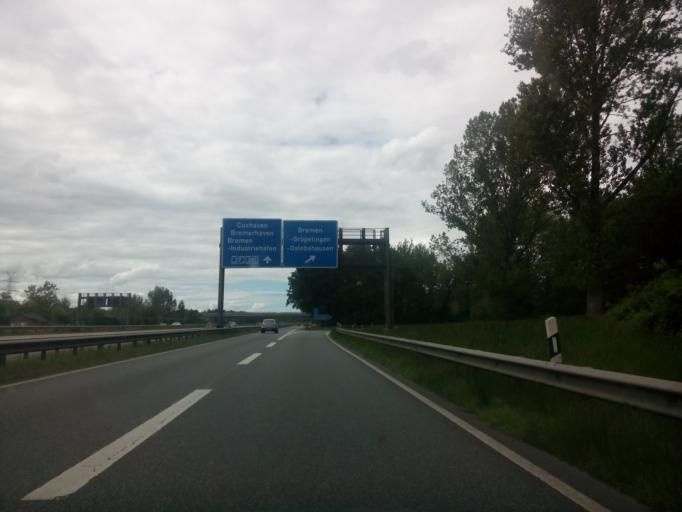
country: DE
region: Lower Saxony
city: Ritterhude
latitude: 53.1441
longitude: 8.7369
